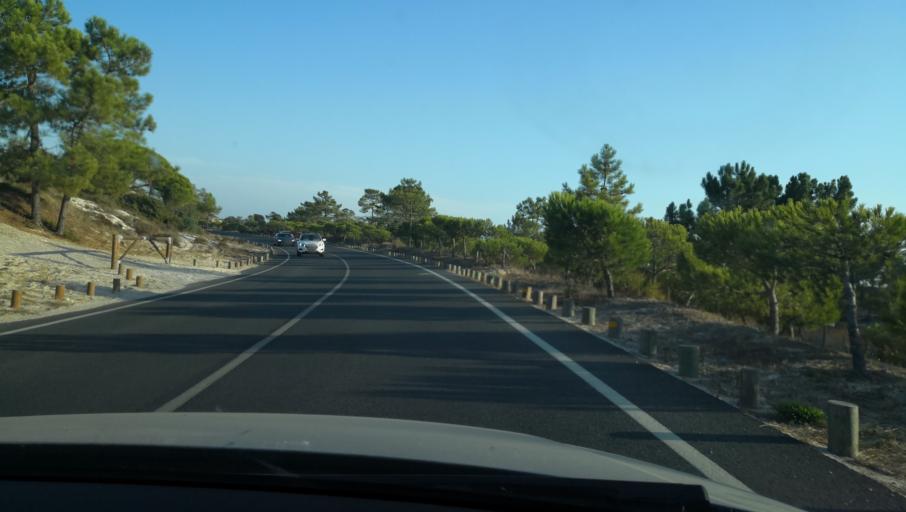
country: PT
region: Setubal
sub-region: Setubal
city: Setubal
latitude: 38.4704
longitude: -8.8841
